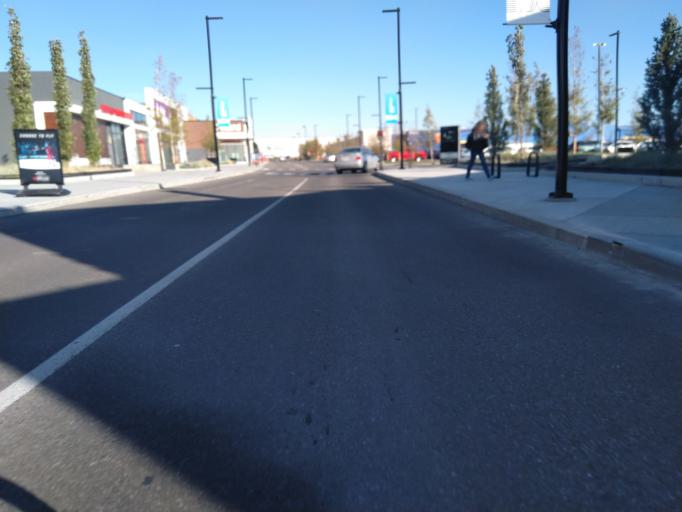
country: CA
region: Alberta
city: Calgary
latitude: 51.1085
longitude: -114.0408
